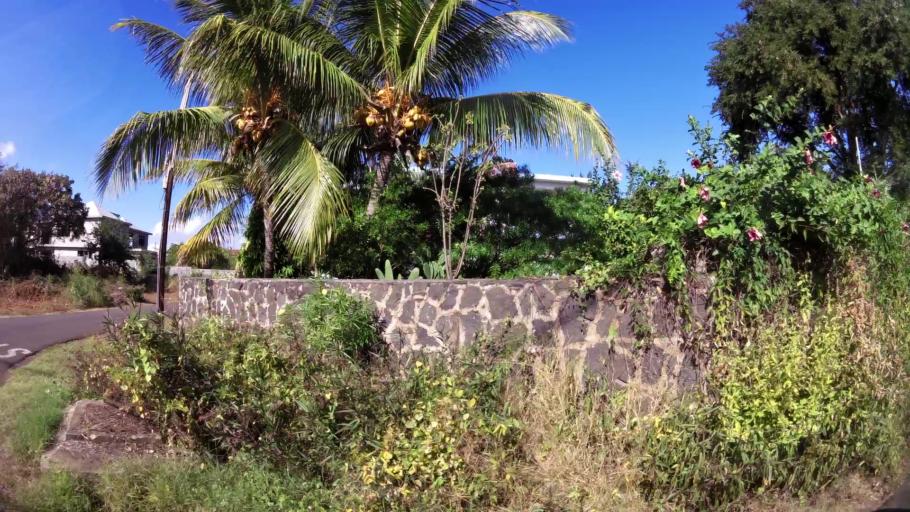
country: MU
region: Black River
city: Albion
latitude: -20.2069
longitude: 57.4064
